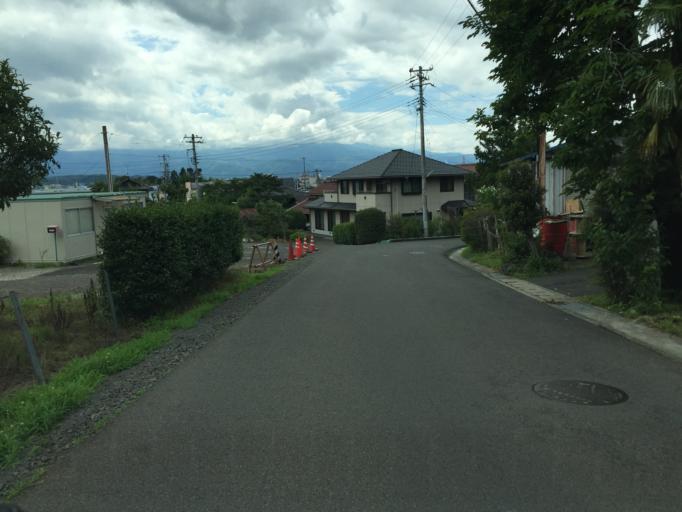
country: JP
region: Fukushima
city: Fukushima-shi
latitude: 37.7323
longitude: 140.4762
